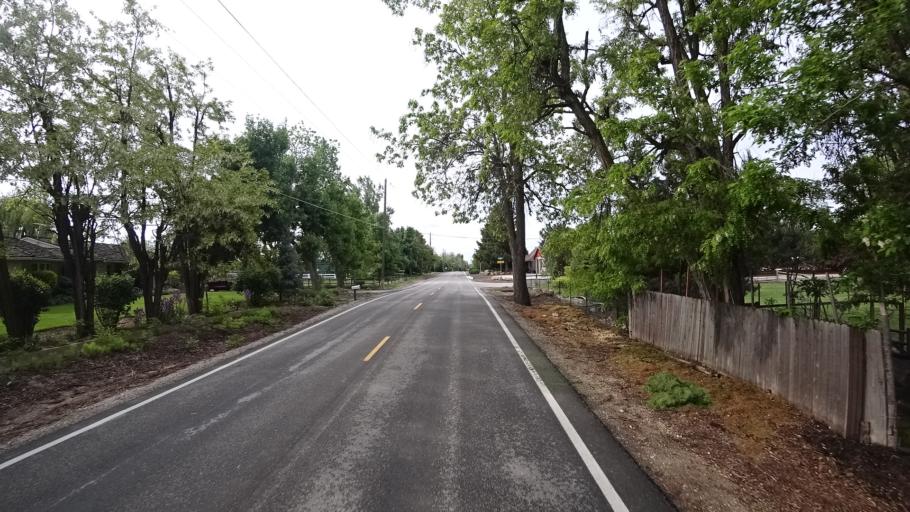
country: US
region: Idaho
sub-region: Ada County
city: Eagle
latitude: 43.7088
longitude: -116.3791
